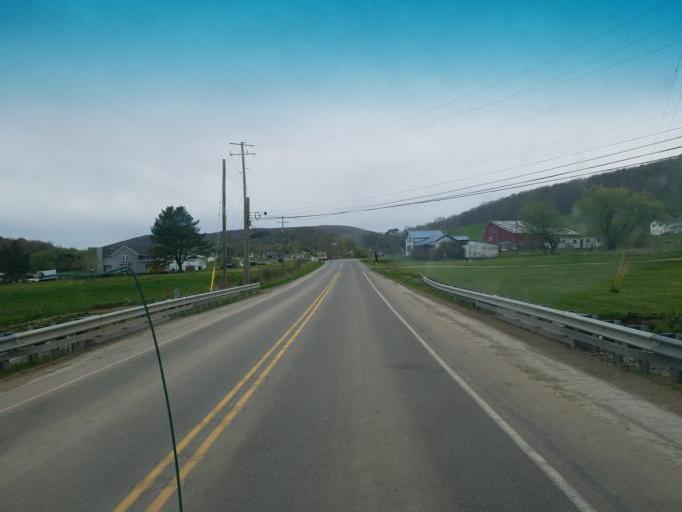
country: US
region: Pennsylvania
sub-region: Tioga County
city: Westfield
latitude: 41.9445
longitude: -77.6726
